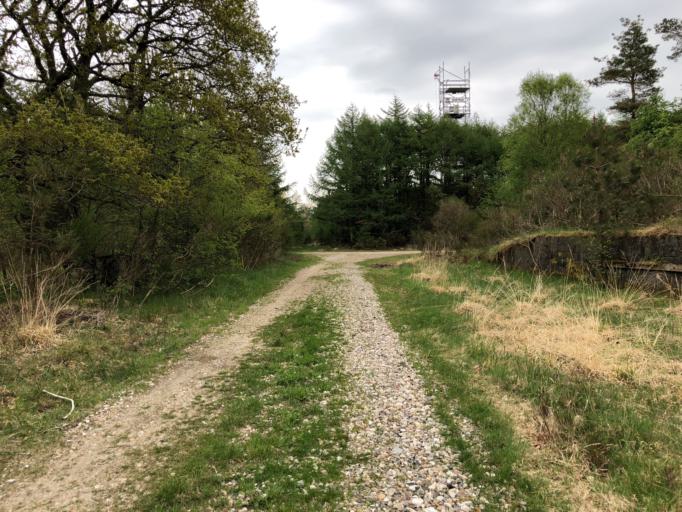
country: DK
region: Central Jutland
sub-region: Holstebro Kommune
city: Ulfborg
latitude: 56.2918
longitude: 8.4270
